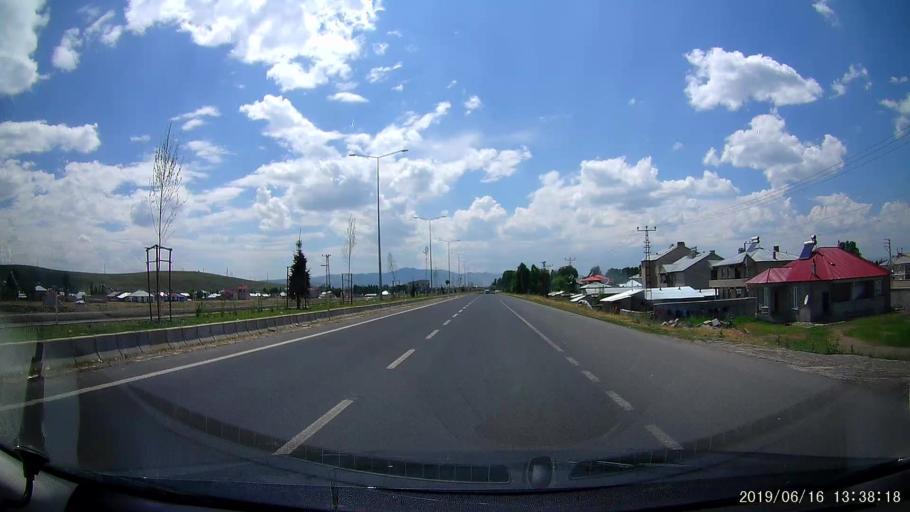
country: TR
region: Agri
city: Agri
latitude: 39.7119
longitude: 43.0759
